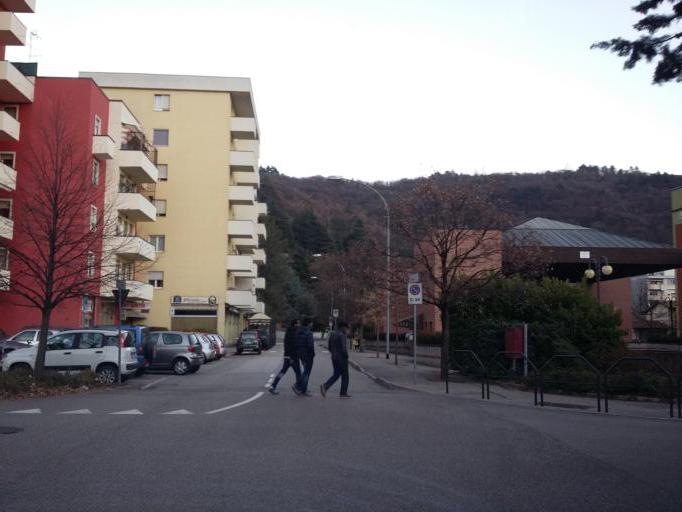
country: IT
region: Trentino-Alto Adige
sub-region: Provincia di Trento
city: Villa Lagarina
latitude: 45.9041
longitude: 11.0427
